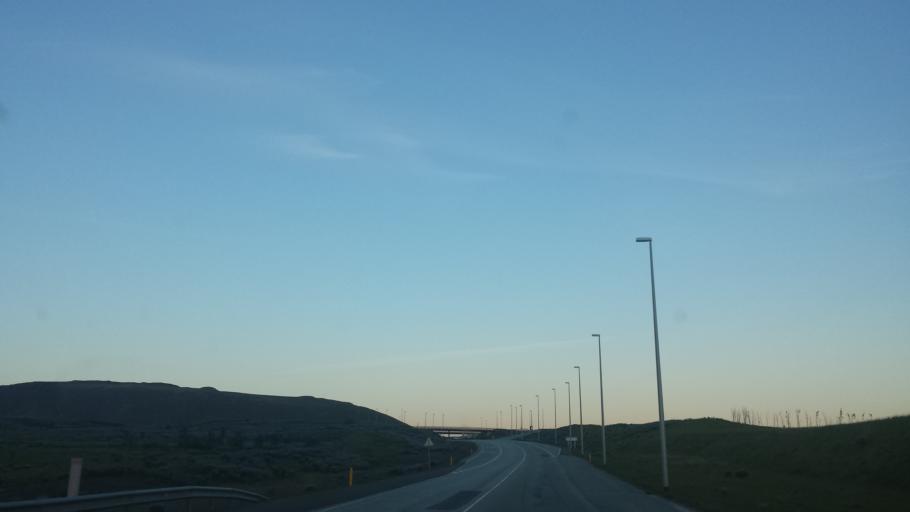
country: IS
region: Capital Region
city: Mosfellsbaer
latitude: 64.1878
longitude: -21.6854
